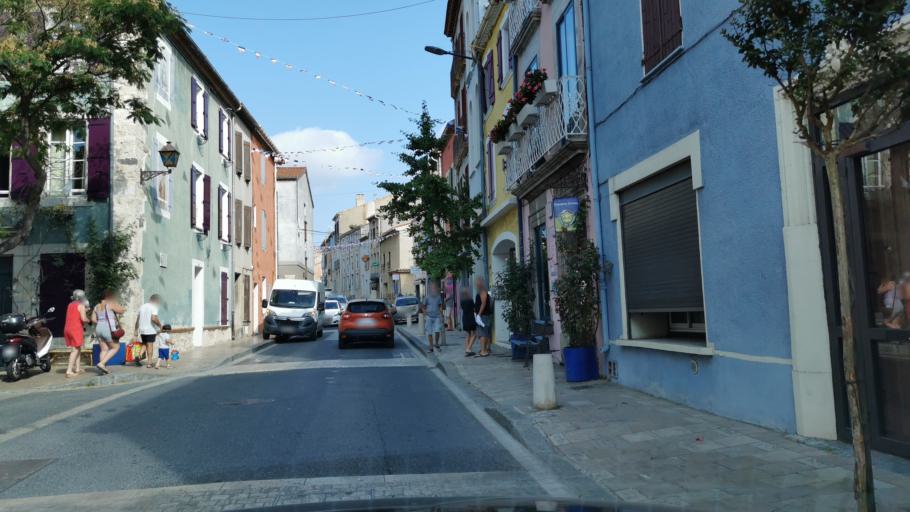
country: FR
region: Languedoc-Roussillon
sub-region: Departement de l'Aude
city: Leucate
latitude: 42.9103
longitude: 3.0283
